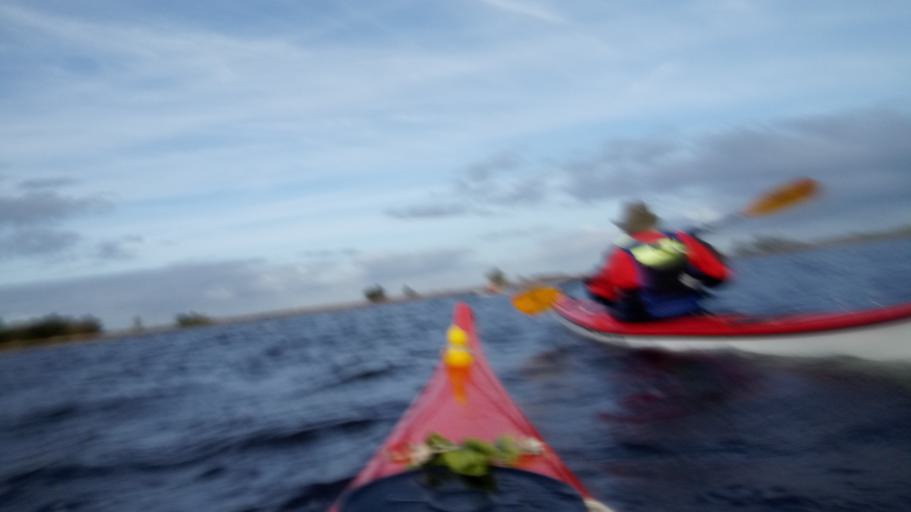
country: NL
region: Overijssel
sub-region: Gemeente Steenwijkerland
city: Sint Jansklooster
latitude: 52.6790
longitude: 6.0307
